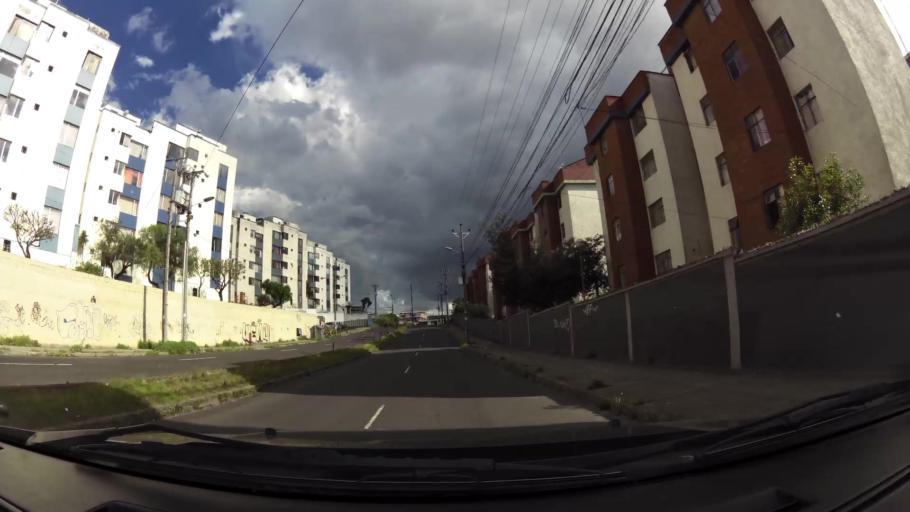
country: EC
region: Pichincha
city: Quito
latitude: -0.1135
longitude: -78.4870
